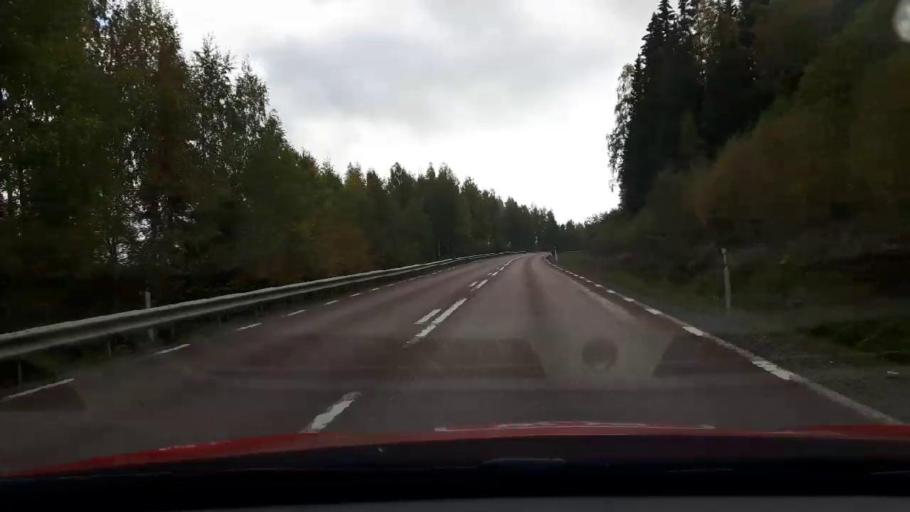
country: SE
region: Gaevleborg
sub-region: Bollnas Kommun
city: Arbra
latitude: 61.5572
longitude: 16.3451
